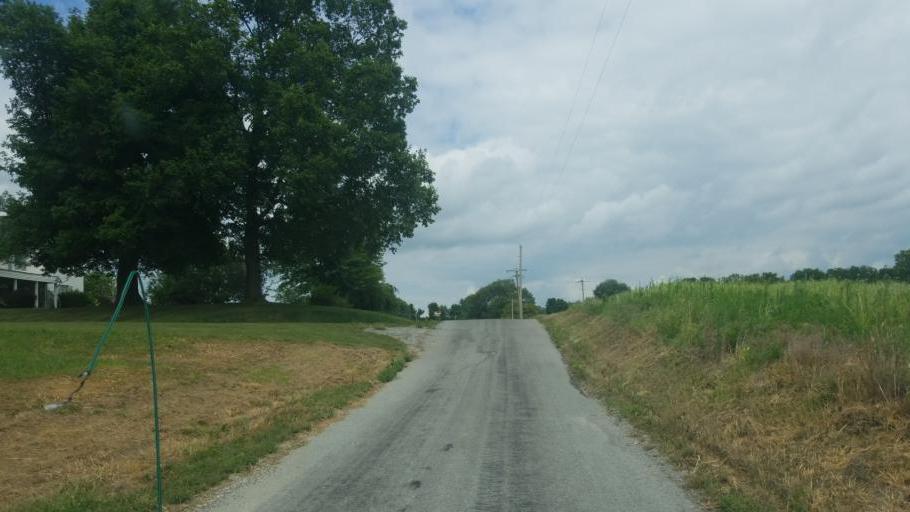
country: US
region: Illinois
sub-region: Jackson County
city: Murphysboro
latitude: 37.7019
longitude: -89.3400
